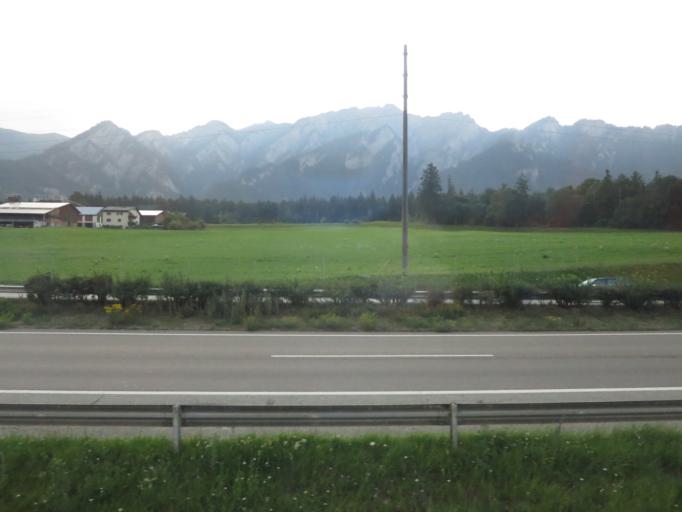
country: CH
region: Grisons
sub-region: Landquart District
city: Trimmis
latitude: 46.8859
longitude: 9.5372
